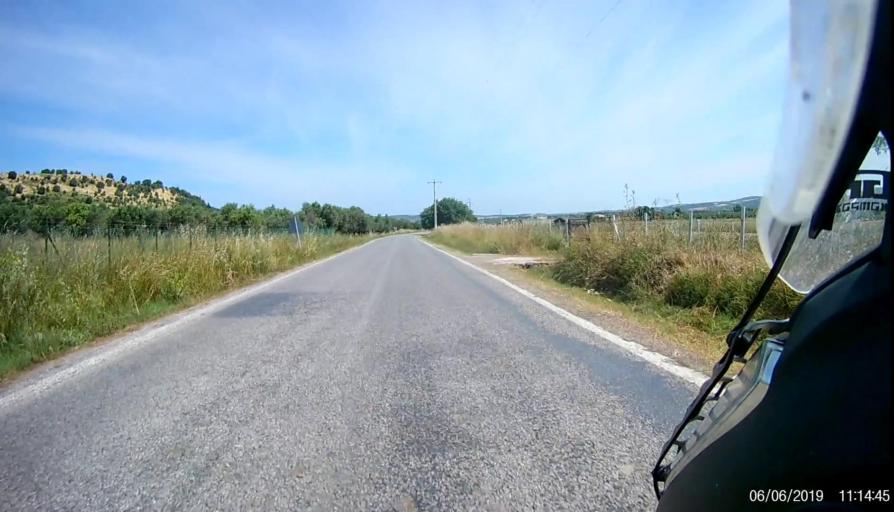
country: TR
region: Canakkale
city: Gulpinar
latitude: 39.6254
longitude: 26.1799
